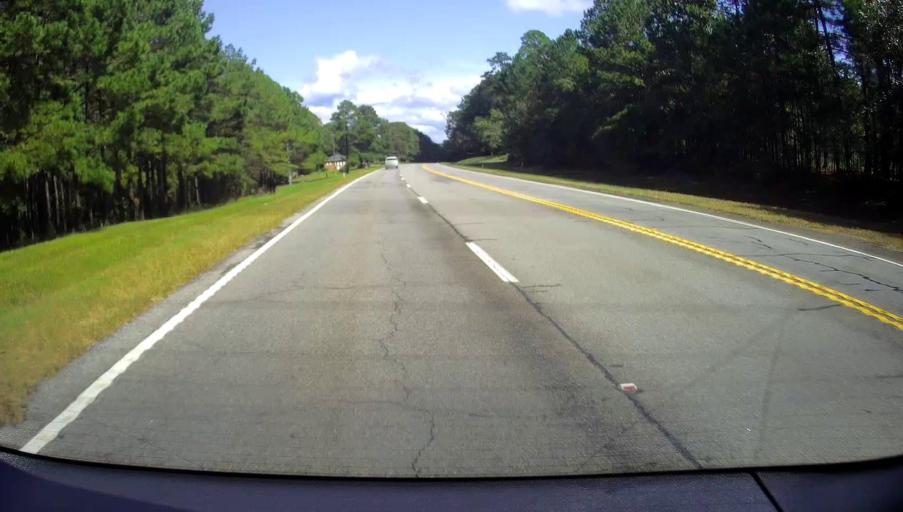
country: US
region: Georgia
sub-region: Jones County
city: Gray
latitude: 33.0259
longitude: -83.4827
